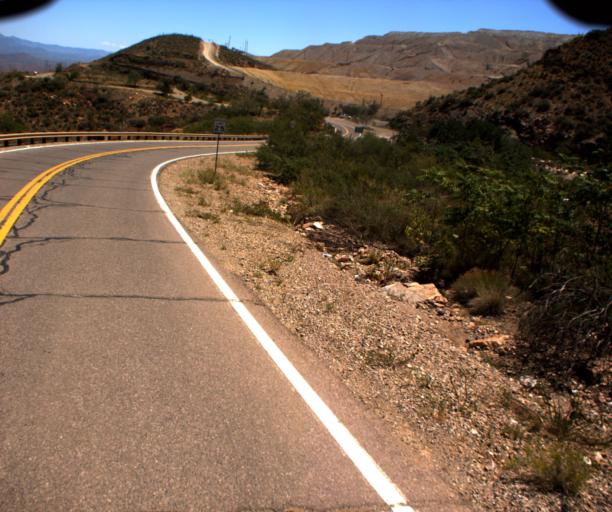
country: US
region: Arizona
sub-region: Greenlee County
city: Morenci
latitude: 33.0735
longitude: -109.3625
